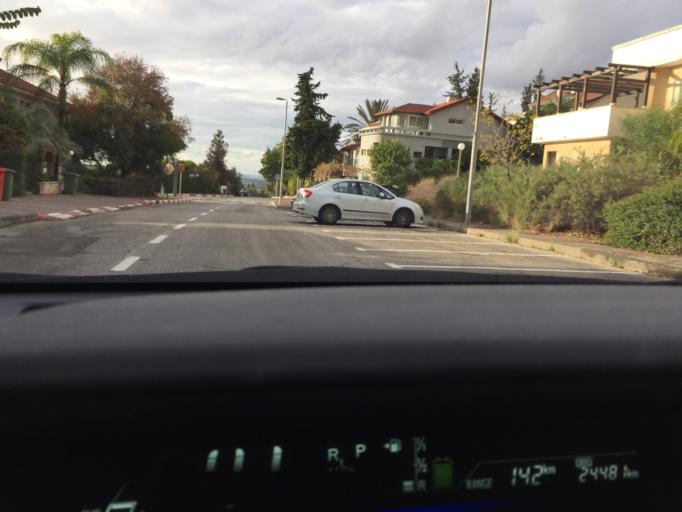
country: PS
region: West Bank
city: Az Zawiyah
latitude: 32.1082
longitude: 35.0342
